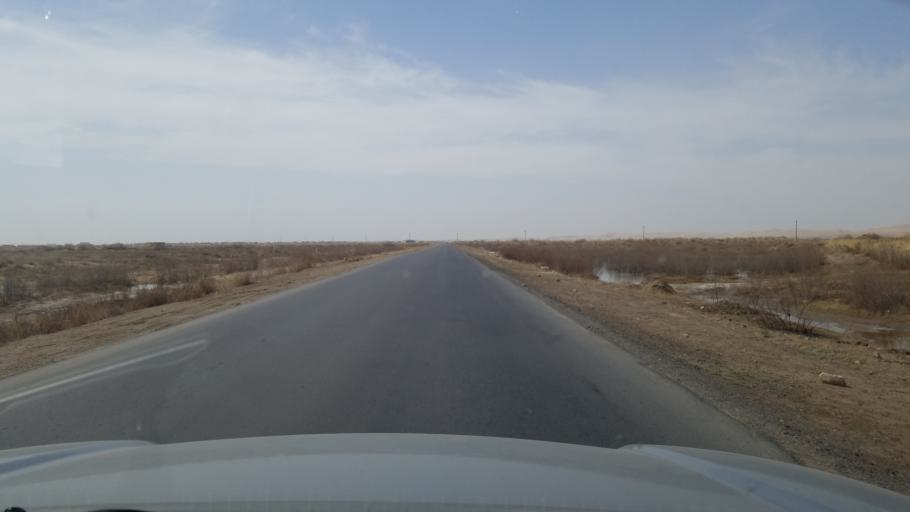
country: TM
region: Lebap
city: Atamyrat
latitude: 37.8343
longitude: 65.3174
